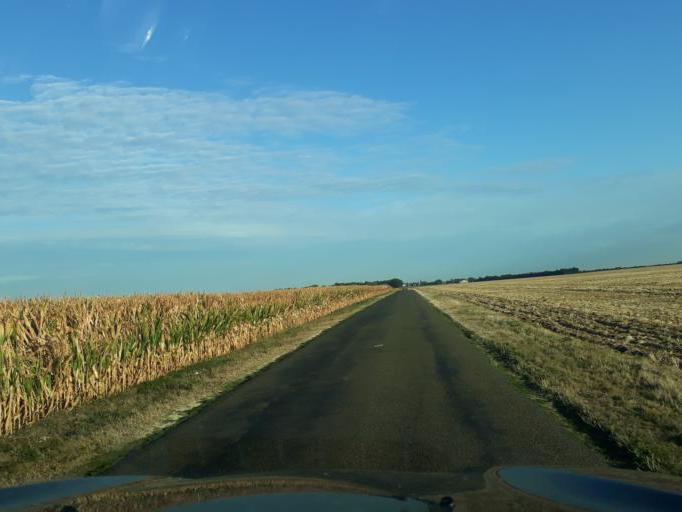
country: FR
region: Centre
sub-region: Departement du Loir-et-Cher
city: Ouzouer-le-Marche
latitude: 47.9523
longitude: 1.5607
